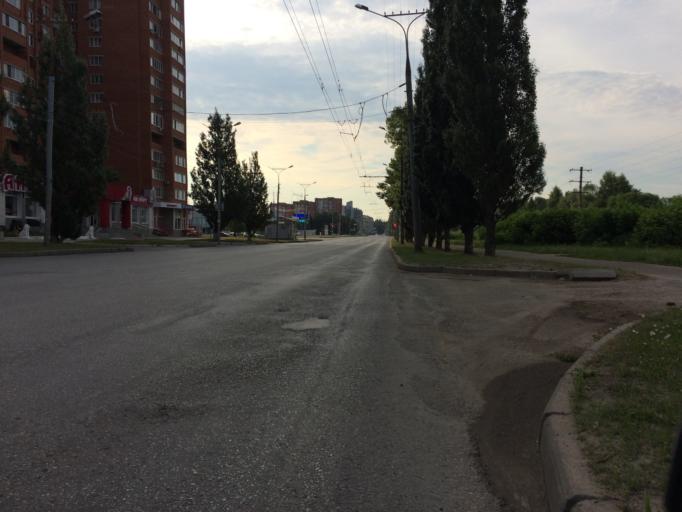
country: RU
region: Mariy-El
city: Yoshkar-Ola
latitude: 56.6257
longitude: 47.9227
